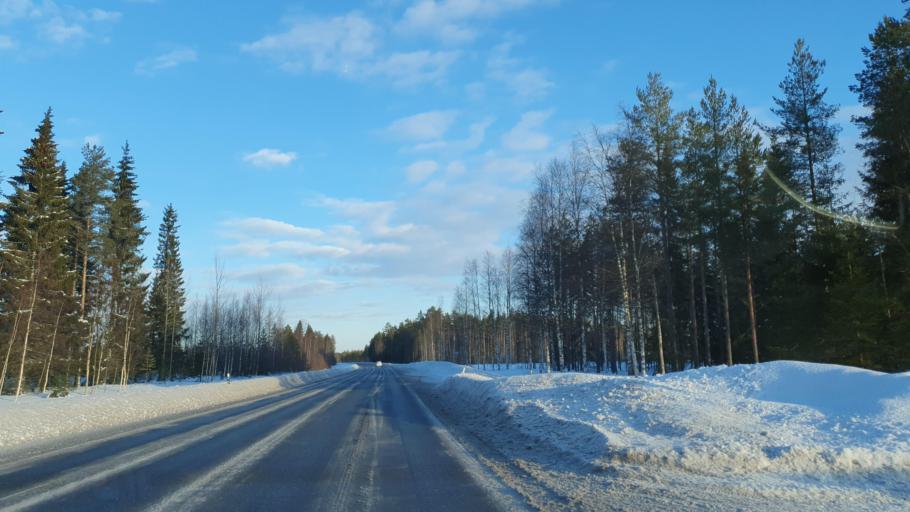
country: FI
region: Northern Ostrobothnia
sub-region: Oulunkaari
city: Utajaervi
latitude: 64.6701
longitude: 26.5403
